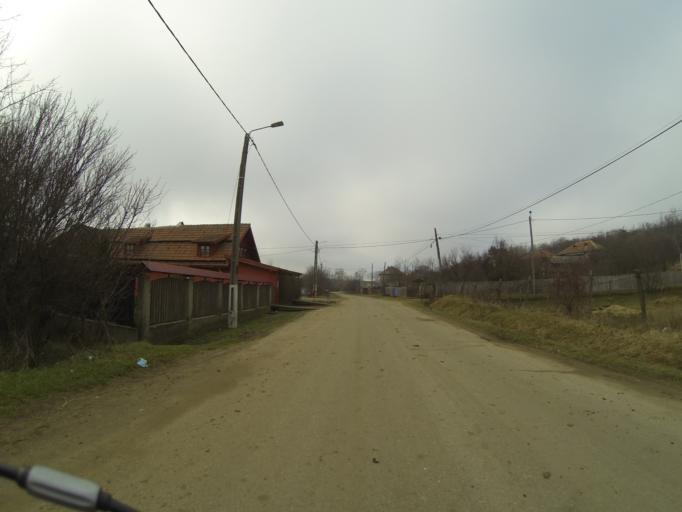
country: RO
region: Mehedinti
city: Padina Mica
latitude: 44.4915
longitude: 23.0044
